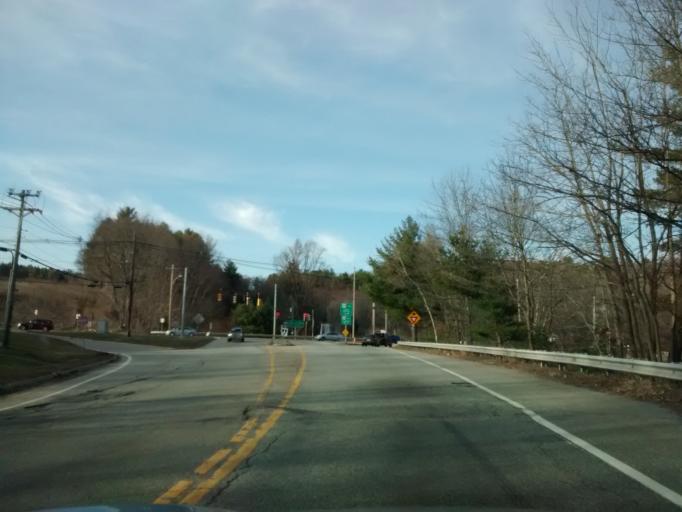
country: US
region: Massachusetts
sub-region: Worcester County
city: Charlton
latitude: 42.1438
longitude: -71.9946
